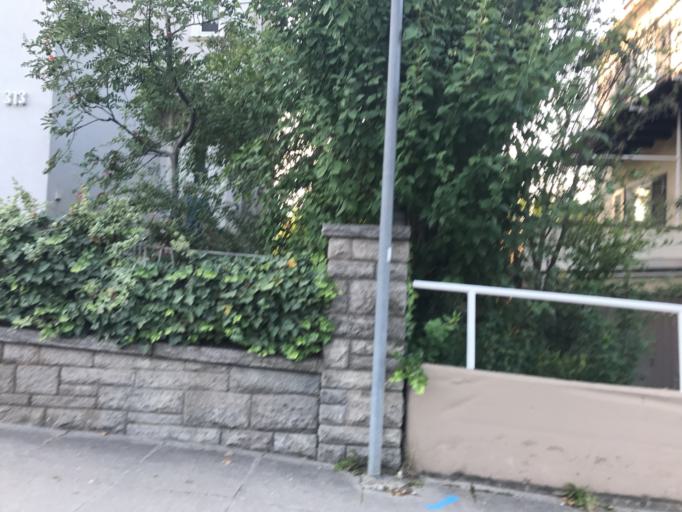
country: DE
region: Baden-Wuerttemberg
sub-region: Regierungsbezirk Stuttgart
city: Korntal
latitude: 48.8196
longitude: 9.1175
